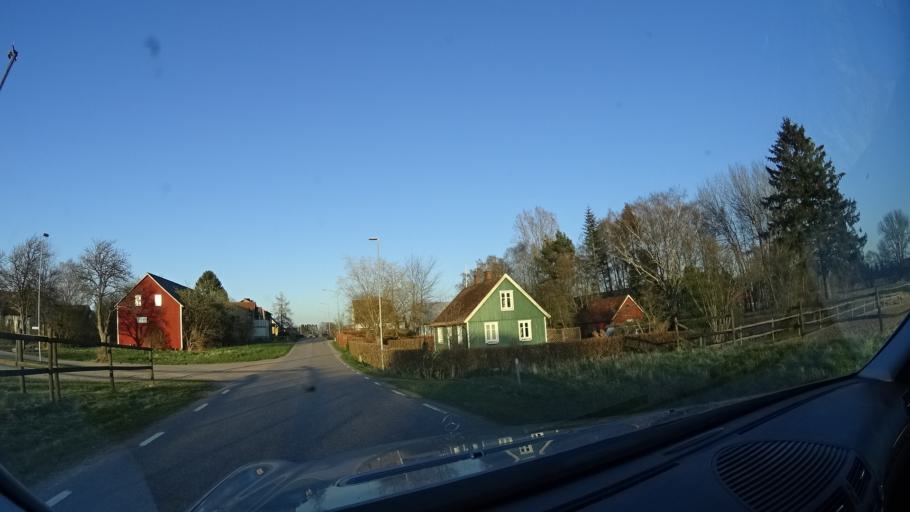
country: SE
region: Skane
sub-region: Eslovs Kommun
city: Stehag
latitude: 55.9618
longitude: 13.3255
